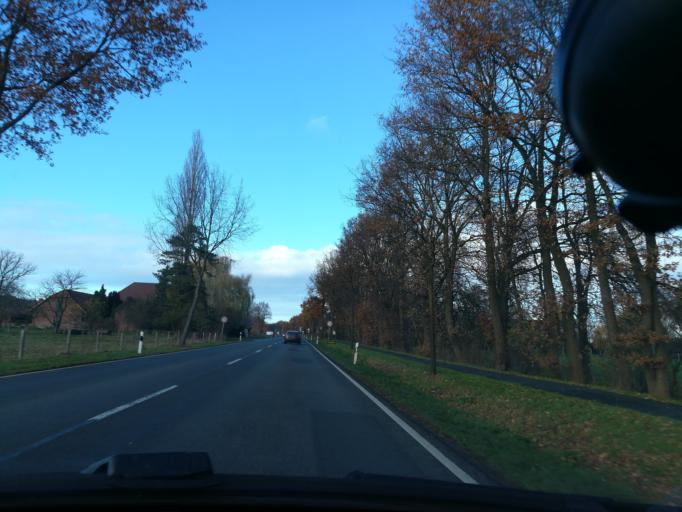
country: DE
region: Lower Saxony
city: Raddestorf
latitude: 52.4493
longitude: 8.9271
